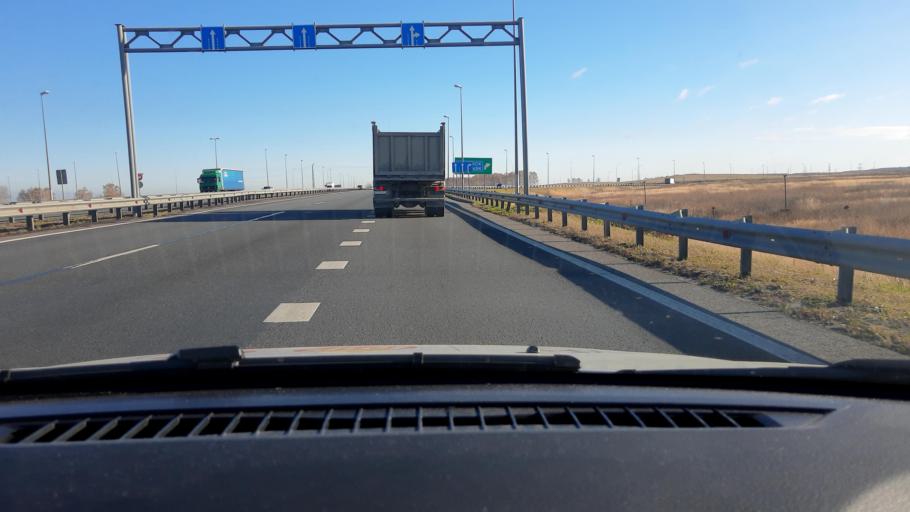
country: RU
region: Nizjnij Novgorod
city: Burevestnik
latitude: 56.1157
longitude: 43.9091
